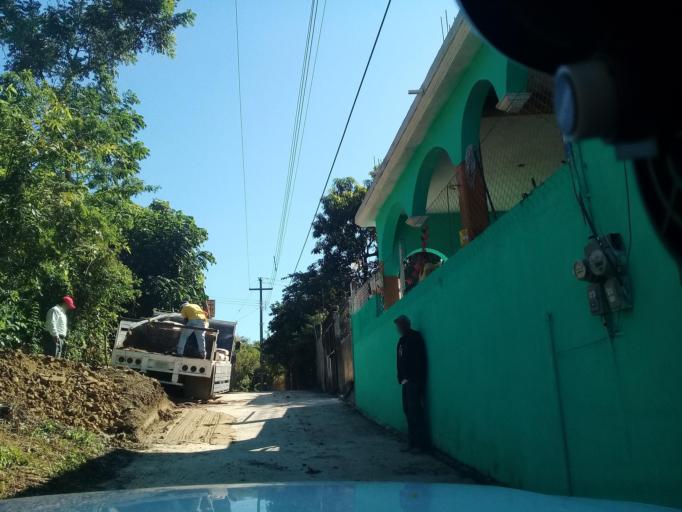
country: MX
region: Hidalgo
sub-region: Huejutla de Reyes
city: Huejutla de Reyes
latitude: 21.1610
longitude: -98.4112
